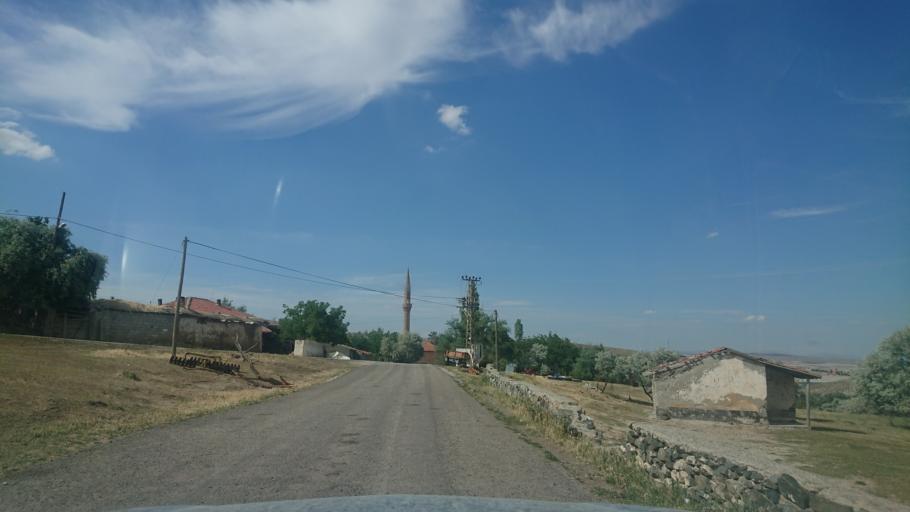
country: TR
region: Aksaray
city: Ortakoy
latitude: 38.8209
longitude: 34.0045
